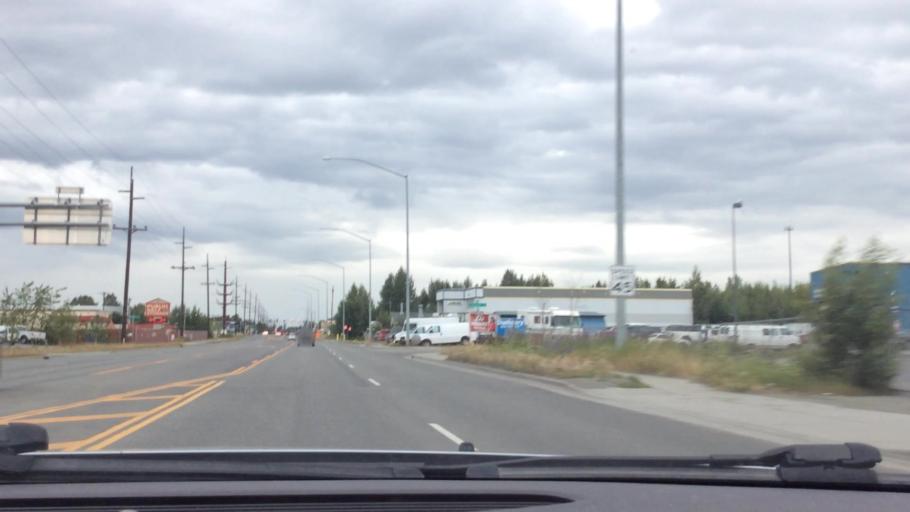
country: US
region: Alaska
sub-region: Anchorage Municipality
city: Anchorage
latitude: 61.1665
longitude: -149.8594
